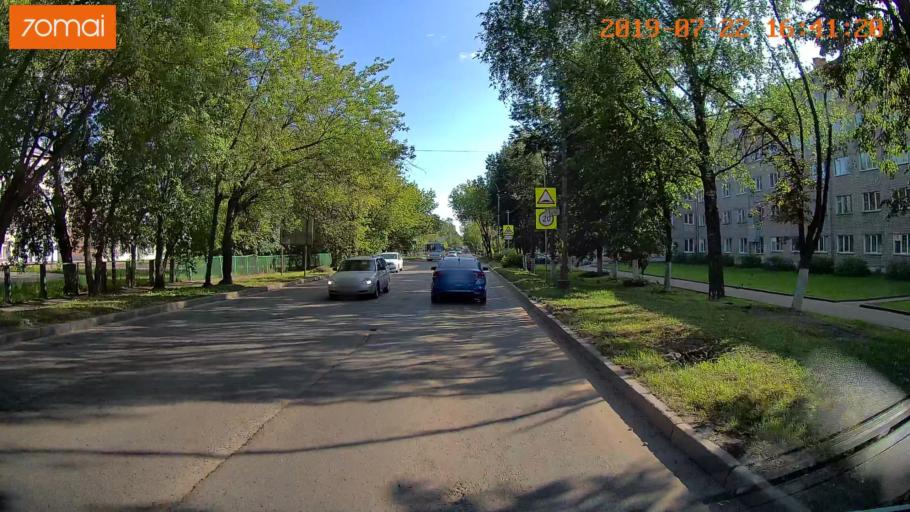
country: RU
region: Ivanovo
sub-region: Gorod Ivanovo
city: Ivanovo
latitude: 57.0219
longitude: 40.9610
